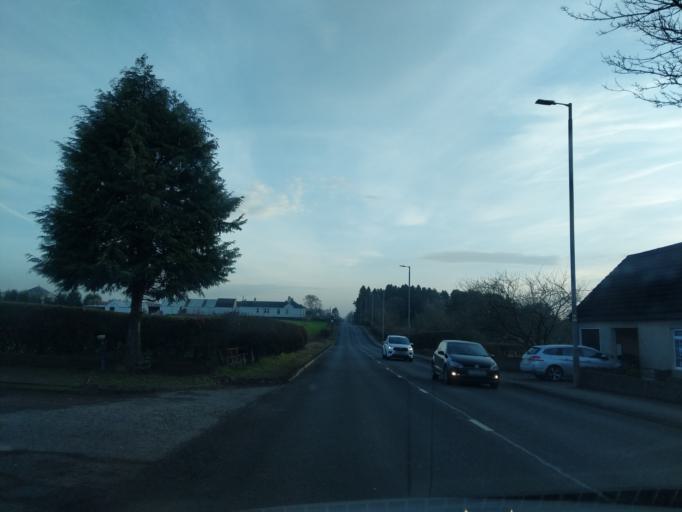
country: GB
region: Scotland
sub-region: South Lanarkshire
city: Carluke
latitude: 55.7232
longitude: -3.8326
